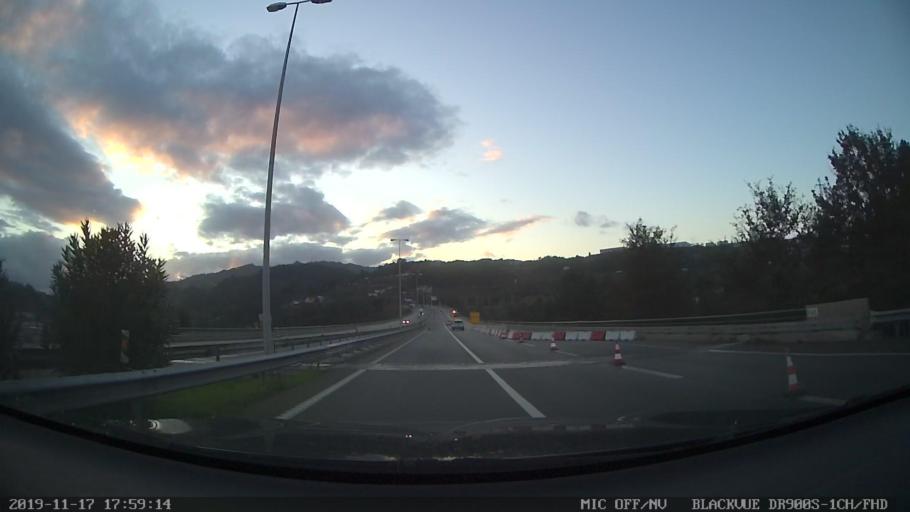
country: PT
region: Porto
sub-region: Amarante
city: Amarante
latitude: 41.2586
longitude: -8.0901
